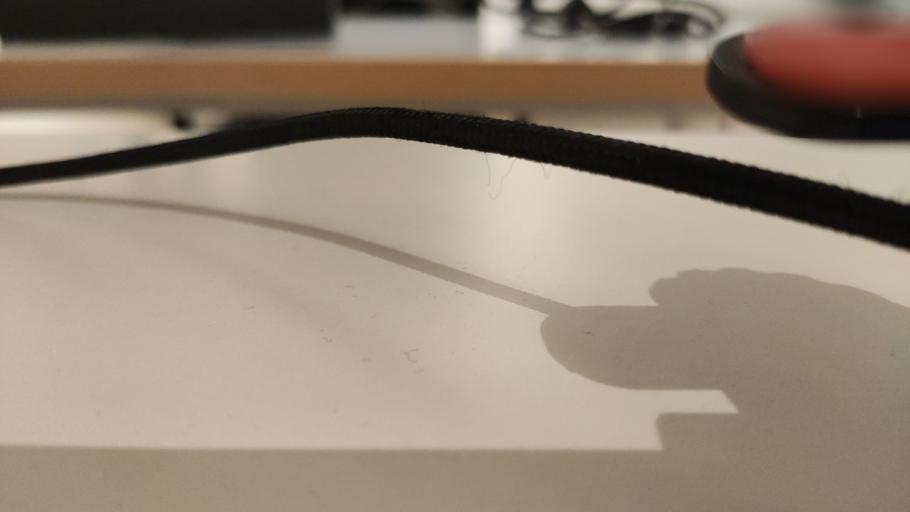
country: RU
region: Moskovskaya
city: Dorokhovo
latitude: 55.4174
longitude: 36.3651
